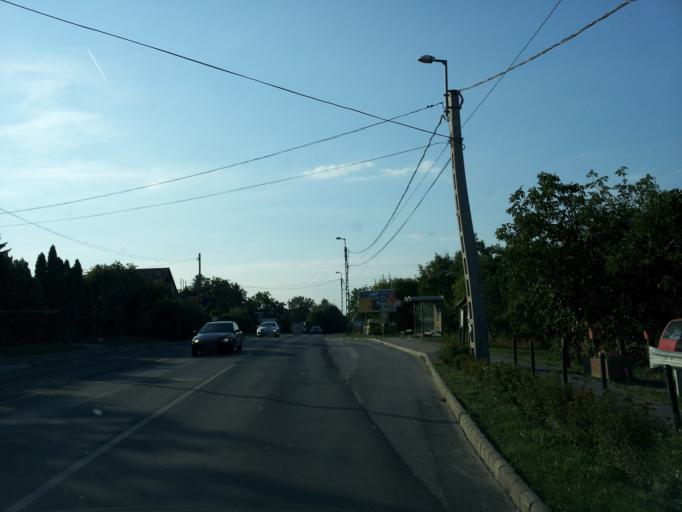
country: HU
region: Pest
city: Tahitotfalu
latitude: 47.7423
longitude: 19.0848
